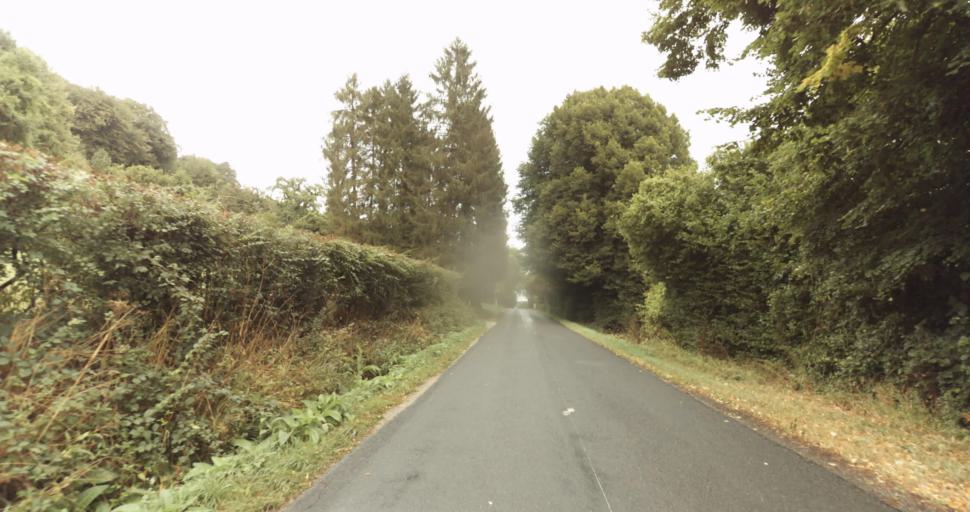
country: FR
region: Lower Normandy
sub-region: Departement de l'Orne
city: Vimoutiers
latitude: 48.9036
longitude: 0.2080
